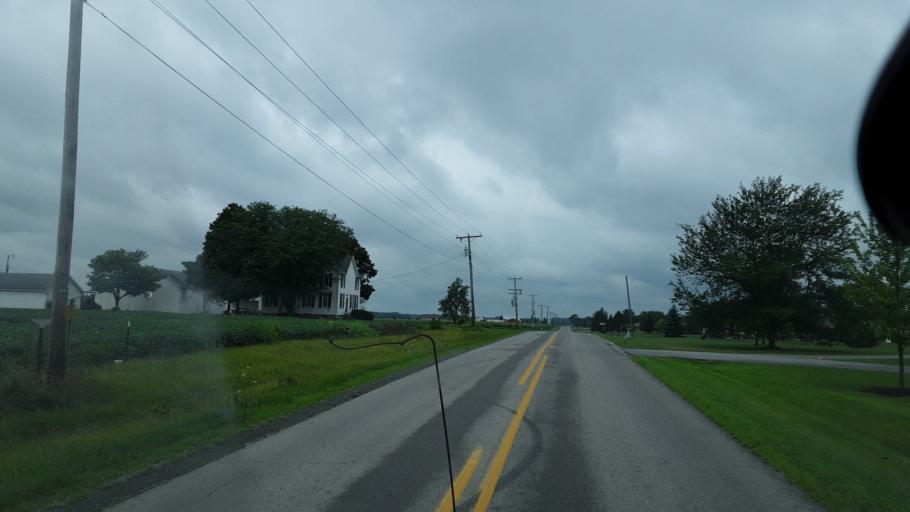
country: US
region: Indiana
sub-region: Allen County
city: New Haven
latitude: 40.9473
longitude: -85.0269
